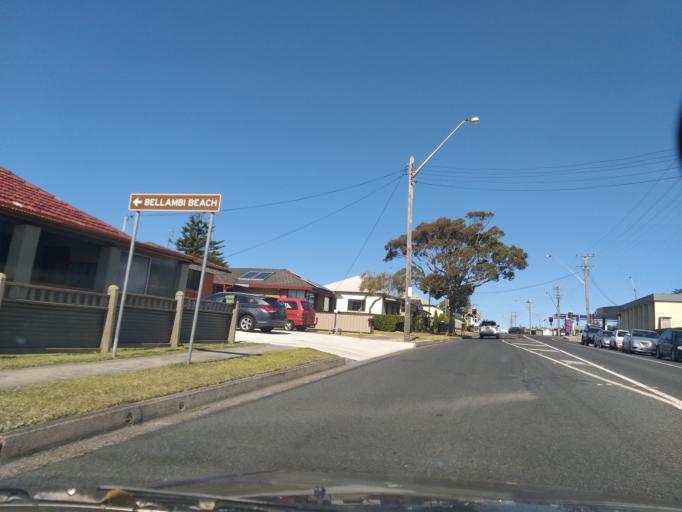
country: AU
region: New South Wales
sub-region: Wollongong
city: East Corrimal
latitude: -34.3671
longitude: 150.9105
